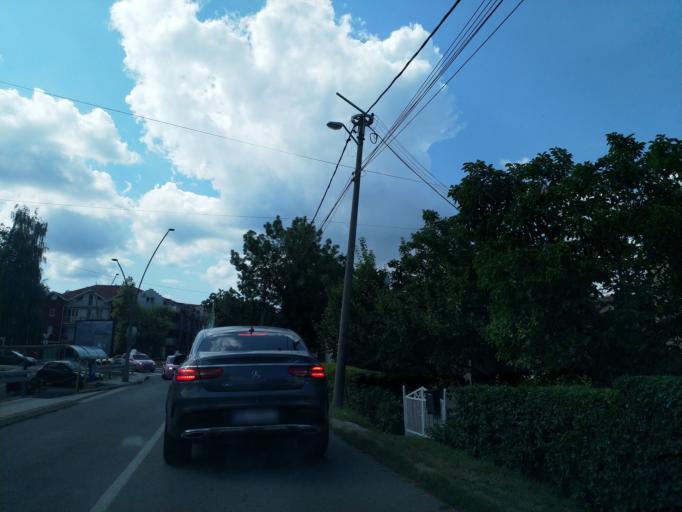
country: RS
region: Central Serbia
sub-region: Raski Okrug
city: Vrnjacka Banja
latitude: 43.6249
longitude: 20.8959
